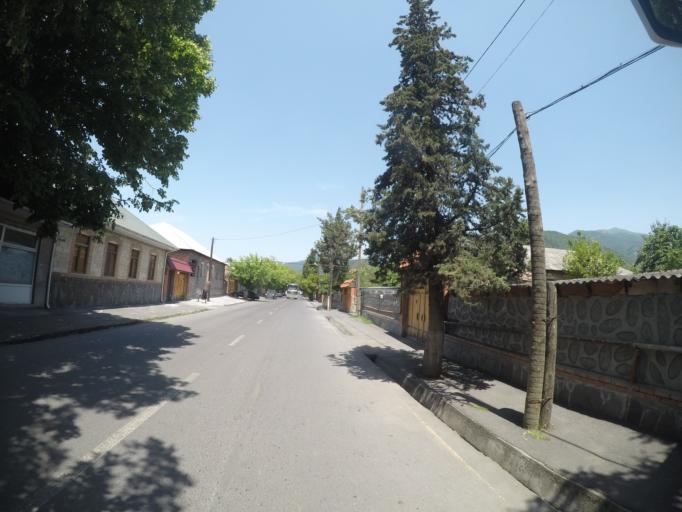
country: AZ
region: Qakh Rayon
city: Qax
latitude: 41.4169
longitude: 46.9196
